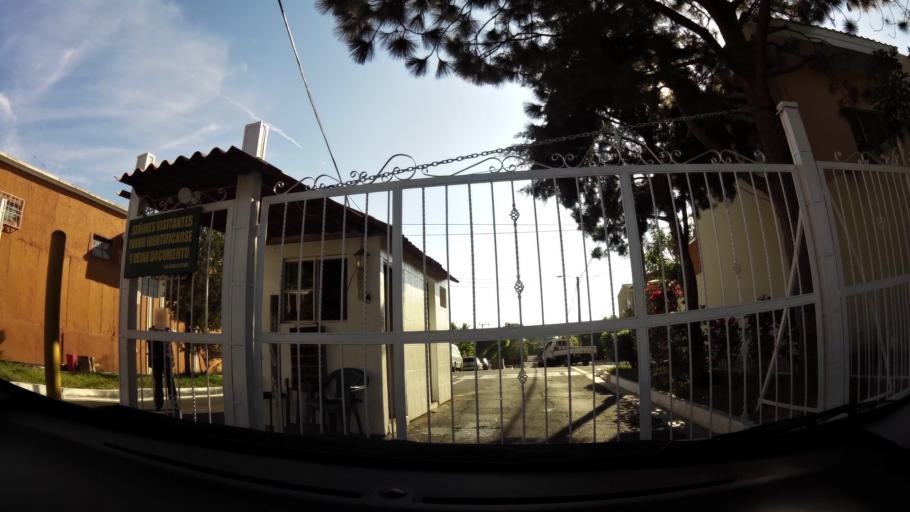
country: SV
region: La Libertad
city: Santa Tecla
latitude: 13.6920
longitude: -89.2874
